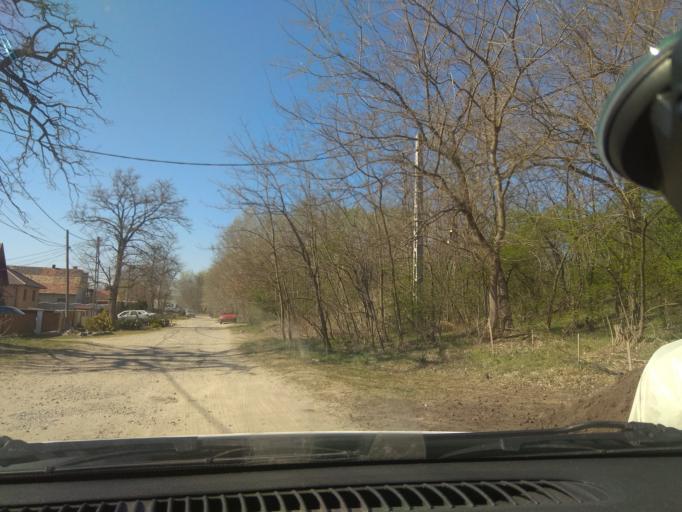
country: HU
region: Pest
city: Szigethalom
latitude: 47.3238
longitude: 19.0145
